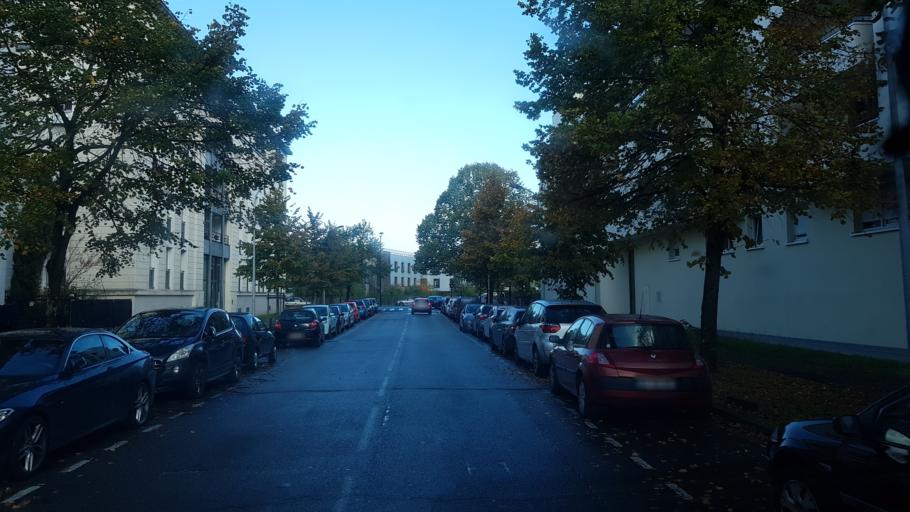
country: FR
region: Aquitaine
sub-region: Departement de la Gironde
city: Le Bouscat
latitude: 44.8662
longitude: -0.5728
